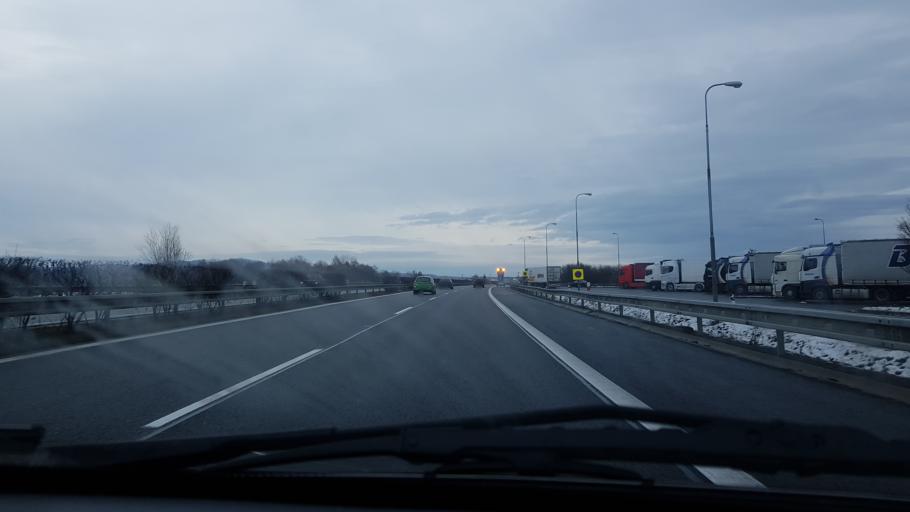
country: CZ
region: Olomoucky
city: Velky Ujezd
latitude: 49.5804
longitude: 17.4620
